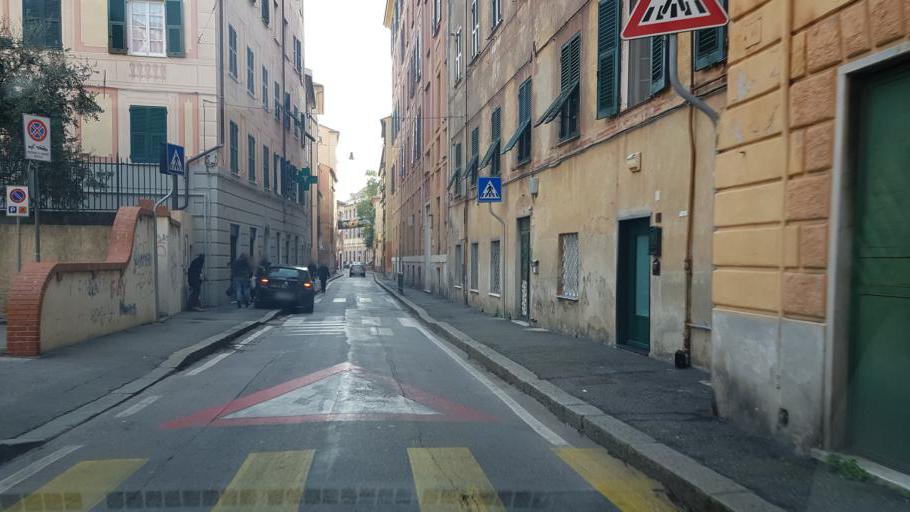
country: IT
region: Liguria
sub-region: Provincia di Genova
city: Bogliasco
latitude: 44.3832
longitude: 9.0439
